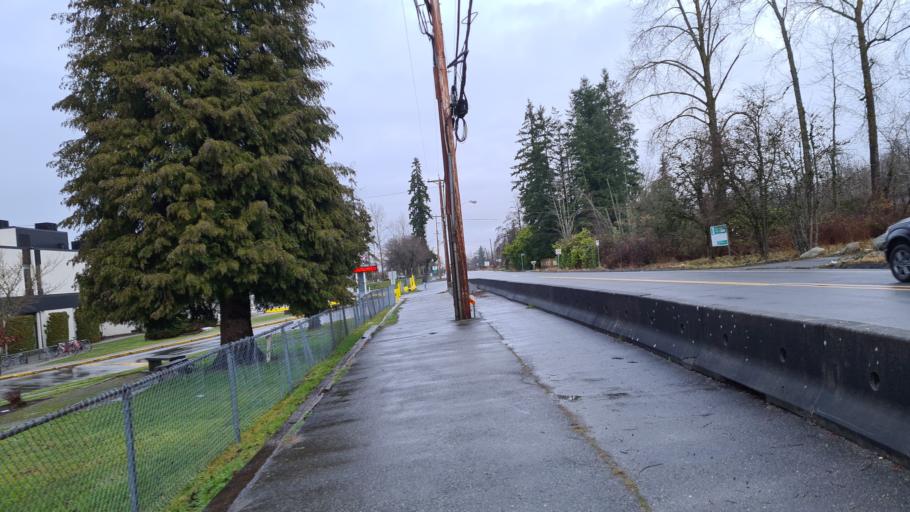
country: CA
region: British Columbia
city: Walnut Grove
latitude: 49.1437
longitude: -122.6616
